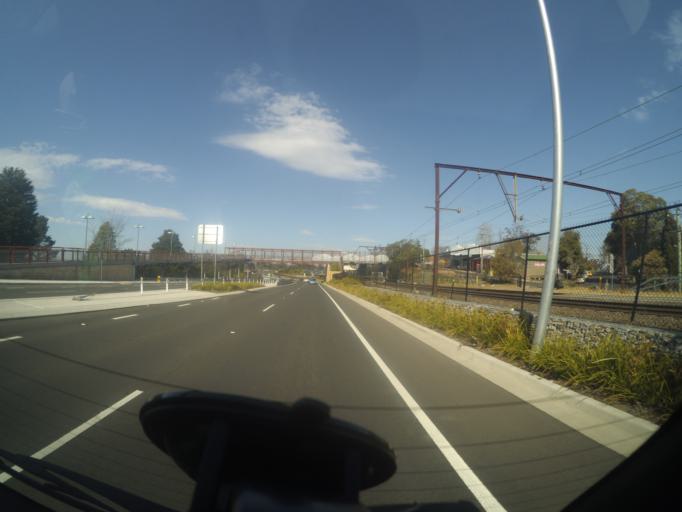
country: AU
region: New South Wales
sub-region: Blue Mountains Municipality
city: Hazelbrook
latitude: -33.7229
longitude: 150.4535
